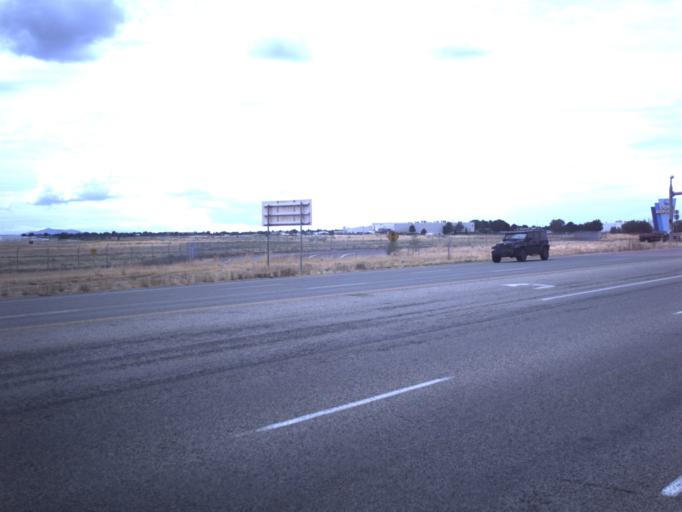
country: US
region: Utah
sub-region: Weber County
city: Riverdale
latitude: 41.2052
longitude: -112.0004
